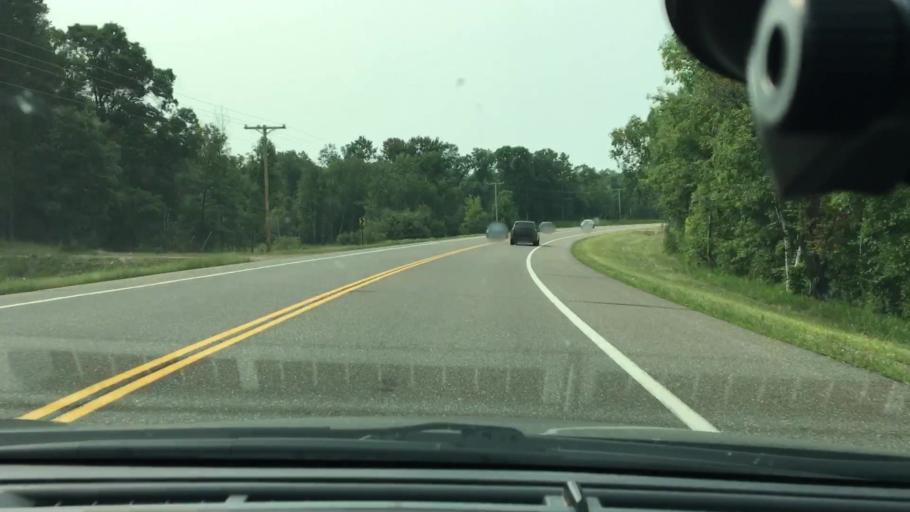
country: US
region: Minnesota
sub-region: Crow Wing County
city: Cross Lake
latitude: 46.5669
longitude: -94.1289
